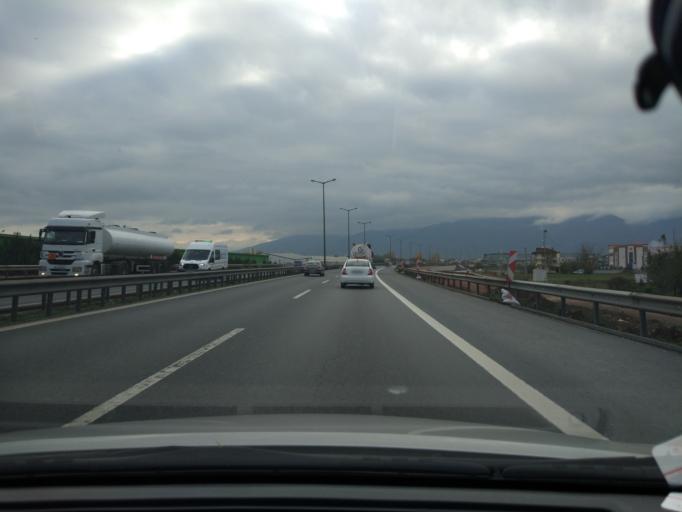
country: TR
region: Kocaeli
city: Kosekoy
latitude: 40.7615
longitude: 30.0335
